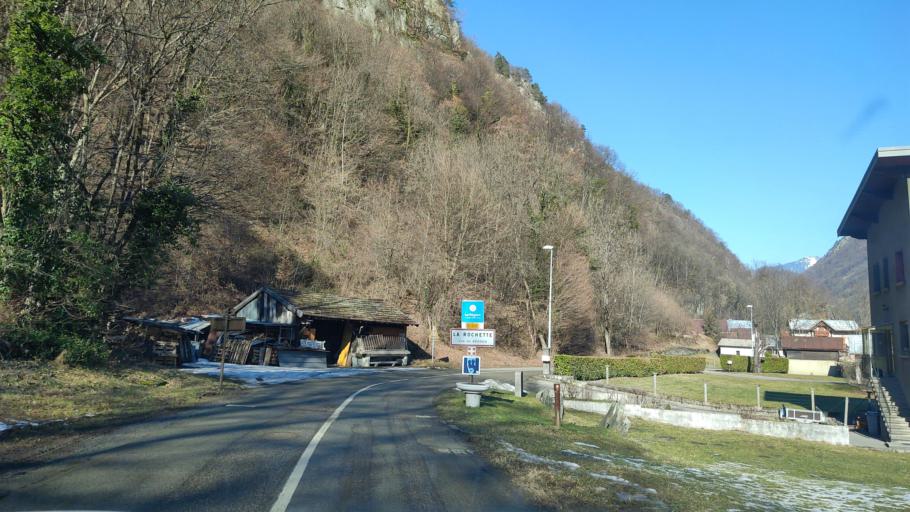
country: FR
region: Rhone-Alpes
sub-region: Departement de la Savoie
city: La Bathie
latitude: 45.5625
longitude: 6.4639
